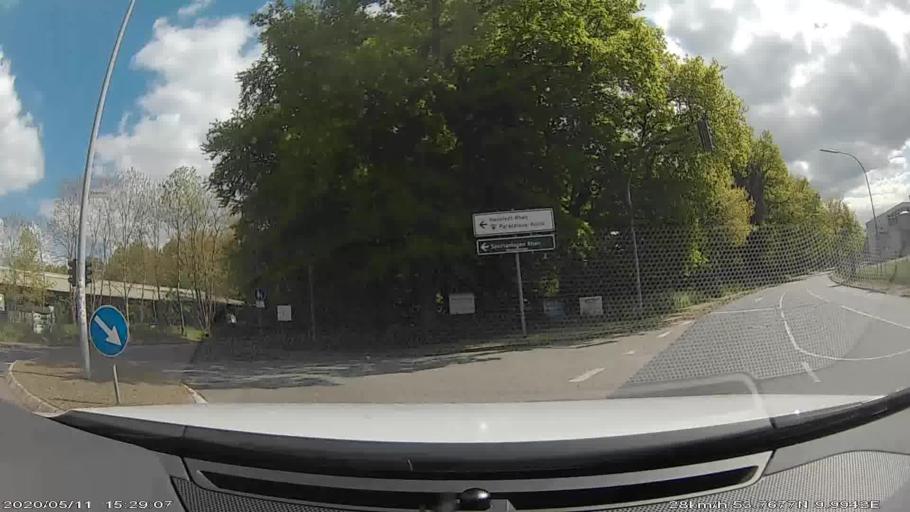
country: DE
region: Schleswig-Holstein
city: Henstedt-Ulzburg
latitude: 53.7587
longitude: 9.9969
